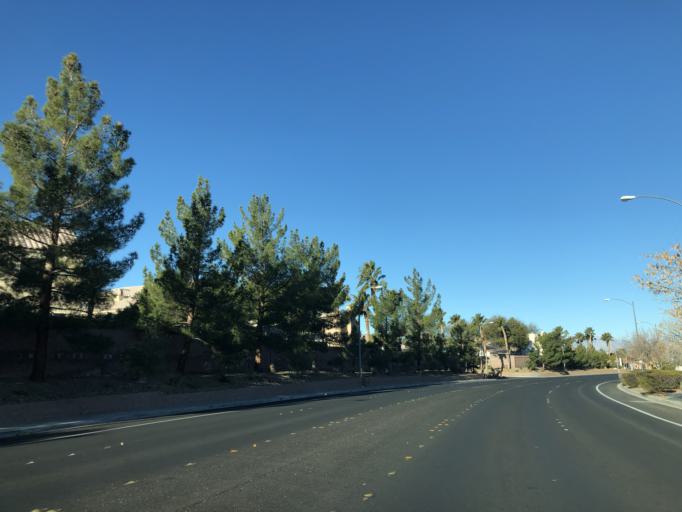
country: US
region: Nevada
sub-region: Clark County
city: Whitney
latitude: 36.0182
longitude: -115.0501
